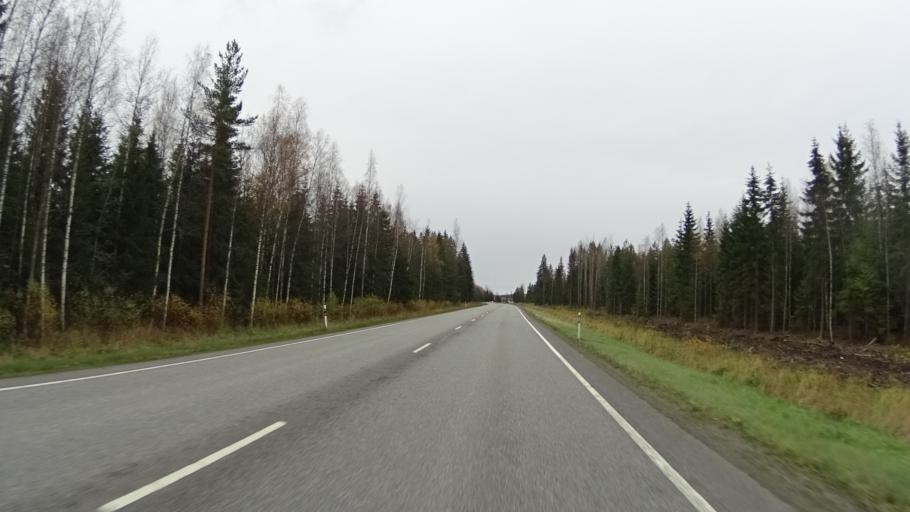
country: FI
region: Kymenlaakso
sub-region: Kouvola
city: Kouvola
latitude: 60.8362
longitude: 26.7920
